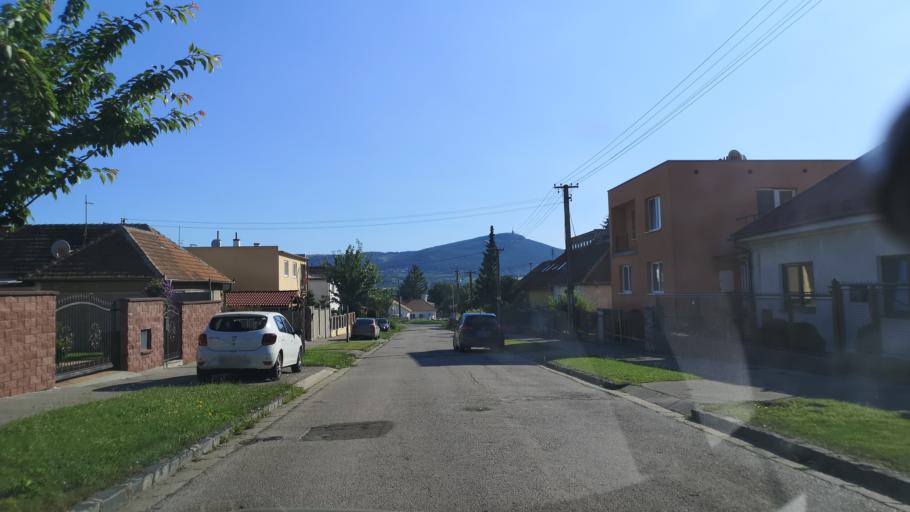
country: SK
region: Nitriansky
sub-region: Okres Nitra
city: Nitra
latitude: 48.3100
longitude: 18.0577
